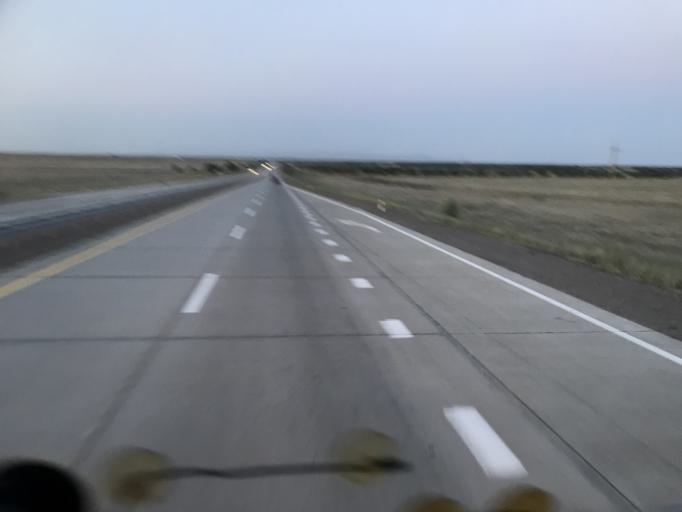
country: KZ
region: Almaty Oblysy
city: Kapshagay
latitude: 43.9720
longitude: 77.3815
